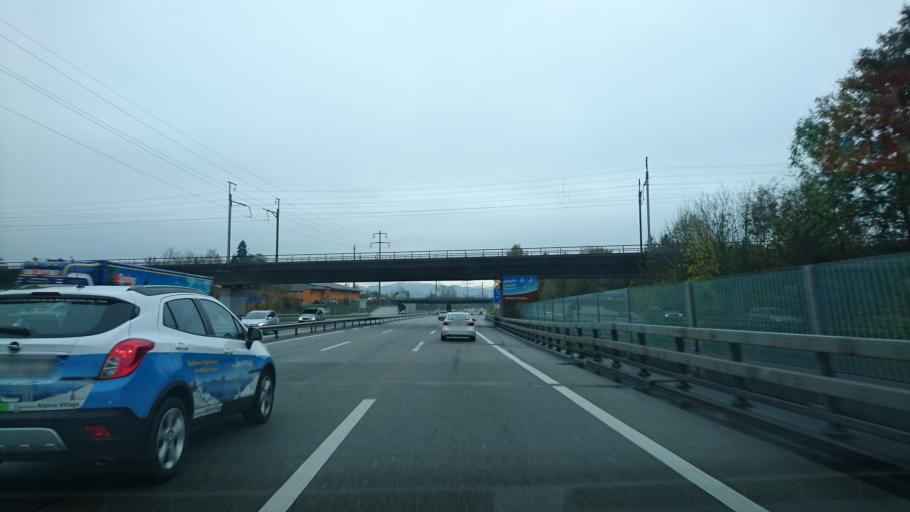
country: CH
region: Aargau
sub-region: Bezirk Zofingen
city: Rothrist
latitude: 47.3129
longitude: 7.8909
